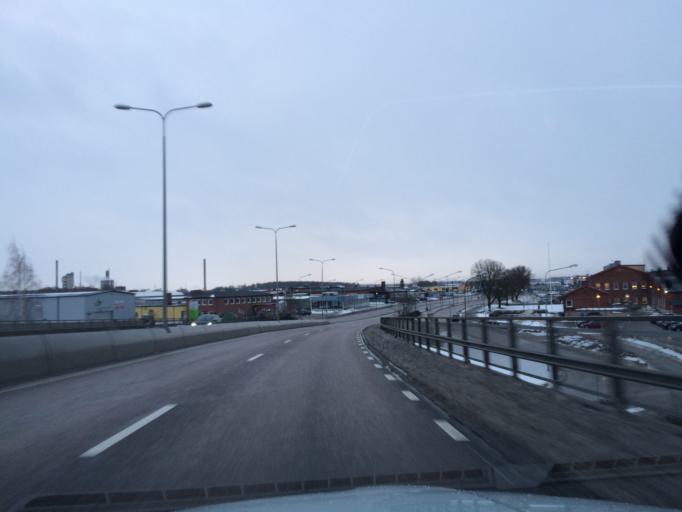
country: SE
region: Vaestmanland
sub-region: Kopings Kommun
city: Koping
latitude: 59.5078
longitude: 15.9937
